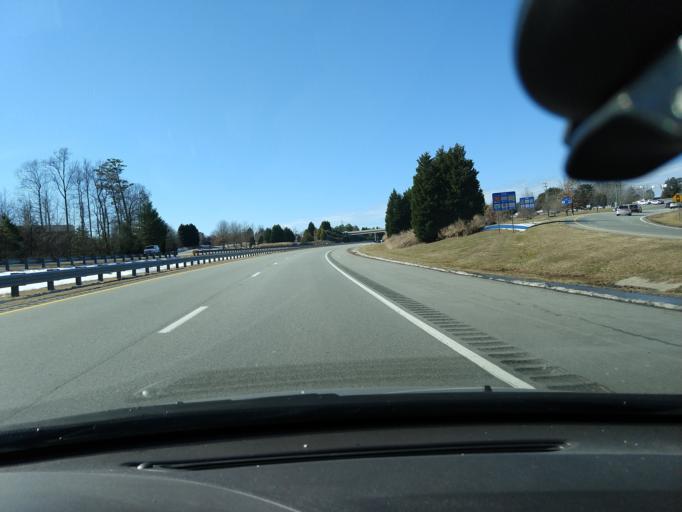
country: US
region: North Carolina
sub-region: Guilford County
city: Greensboro
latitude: 36.1158
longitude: -79.8740
